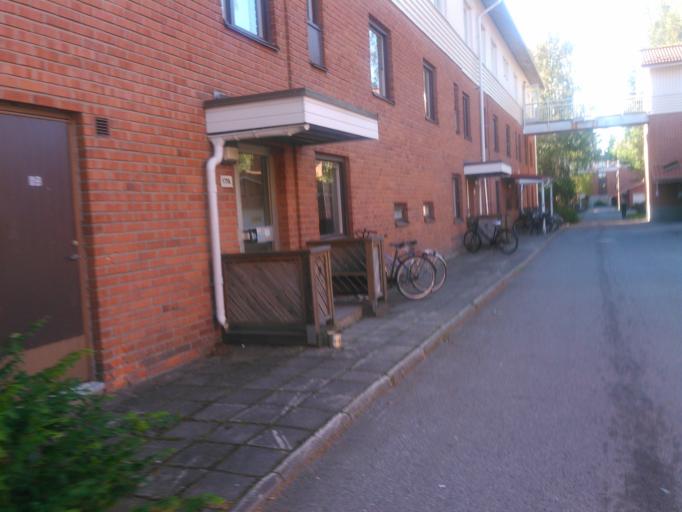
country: SE
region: Vaesterbotten
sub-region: Umea Kommun
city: Umea
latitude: 63.8116
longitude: 20.3104
